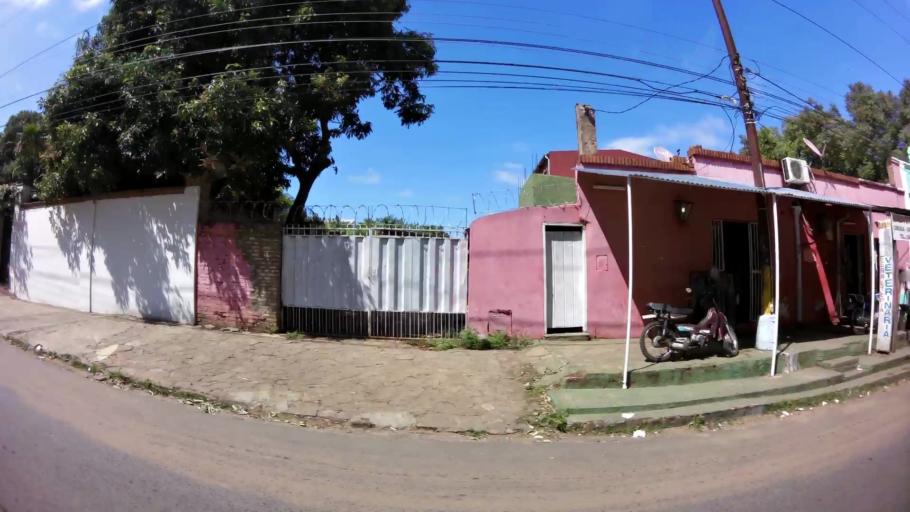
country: PY
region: Central
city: San Lorenzo
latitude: -25.2664
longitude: -57.4863
